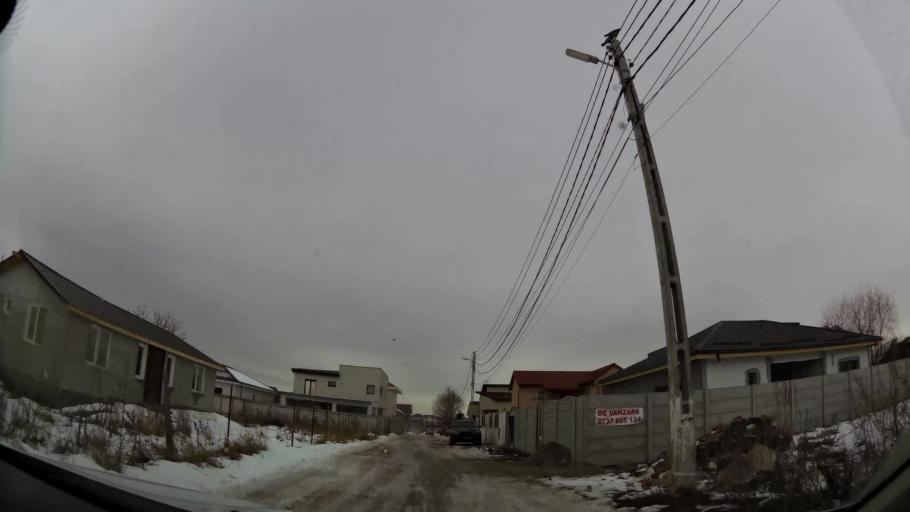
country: RO
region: Ilfov
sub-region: Comuna Pantelimon
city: Pantelimon
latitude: 44.4557
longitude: 26.2203
